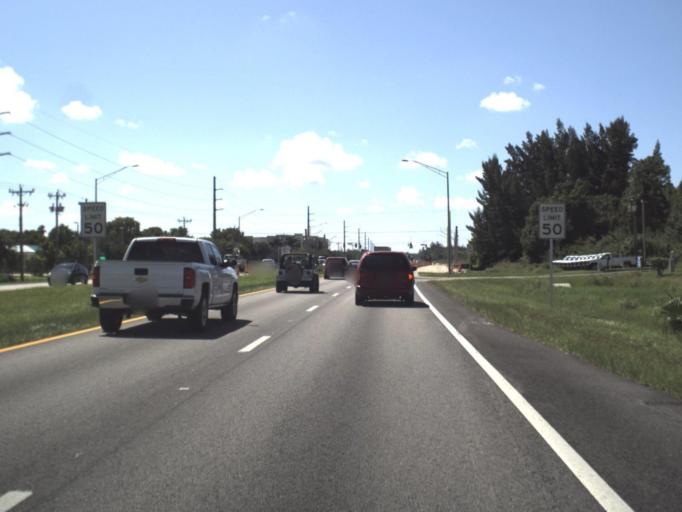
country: US
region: Florida
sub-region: Lee County
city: Lochmoor Waterway Estates
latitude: 26.6519
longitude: -81.9751
